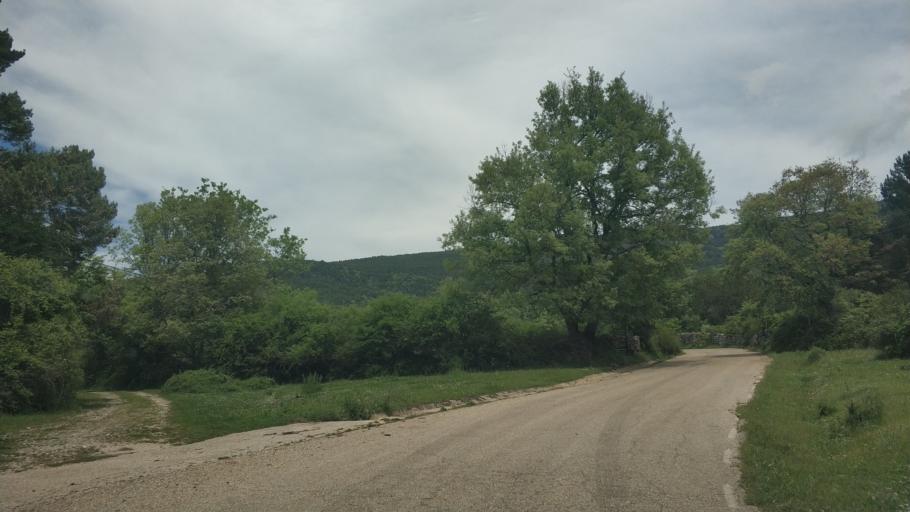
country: ES
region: Castille and Leon
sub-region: Provincia de Soria
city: Vinuesa
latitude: 41.9706
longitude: -2.7805
